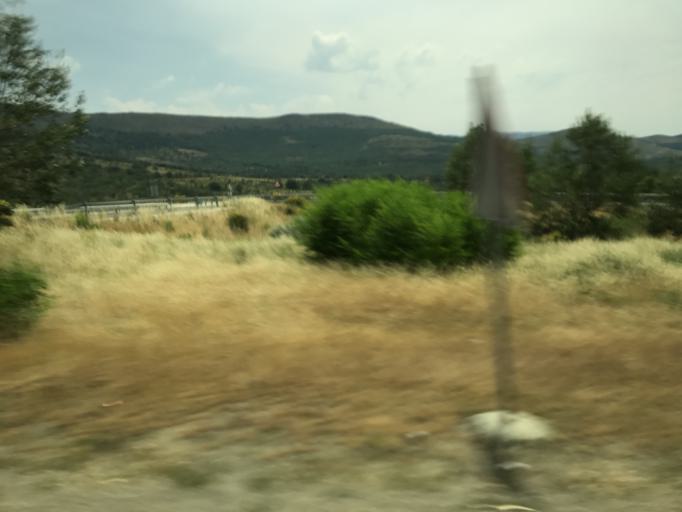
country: ES
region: Madrid
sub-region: Provincia de Madrid
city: Robregordo
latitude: 41.0959
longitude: -3.5935
